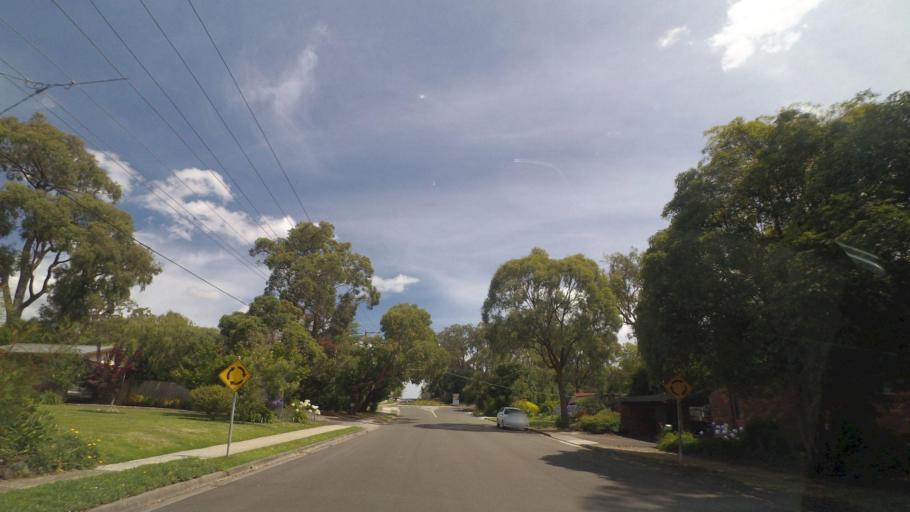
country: AU
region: Victoria
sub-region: Maroondah
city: Bayswater North
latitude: -37.8440
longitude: 145.2924
